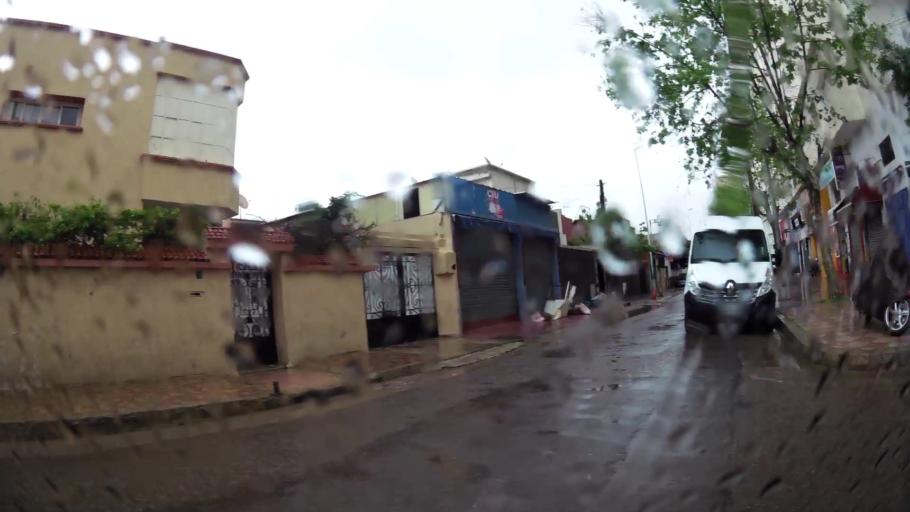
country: MA
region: Grand Casablanca
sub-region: Casablanca
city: Casablanca
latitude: 33.5726
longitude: -7.6294
